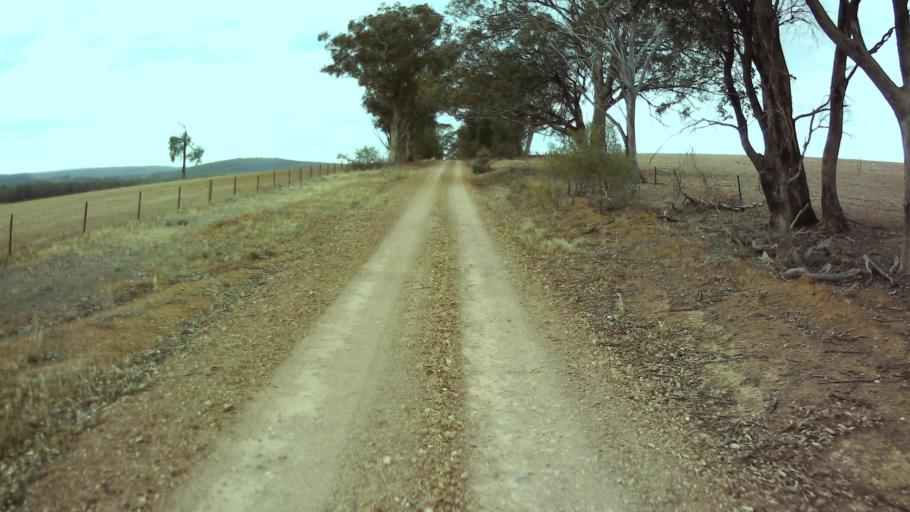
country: AU
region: New South Wales
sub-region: Weddin
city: Grenfell
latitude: -33.9273
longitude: 148.2511
